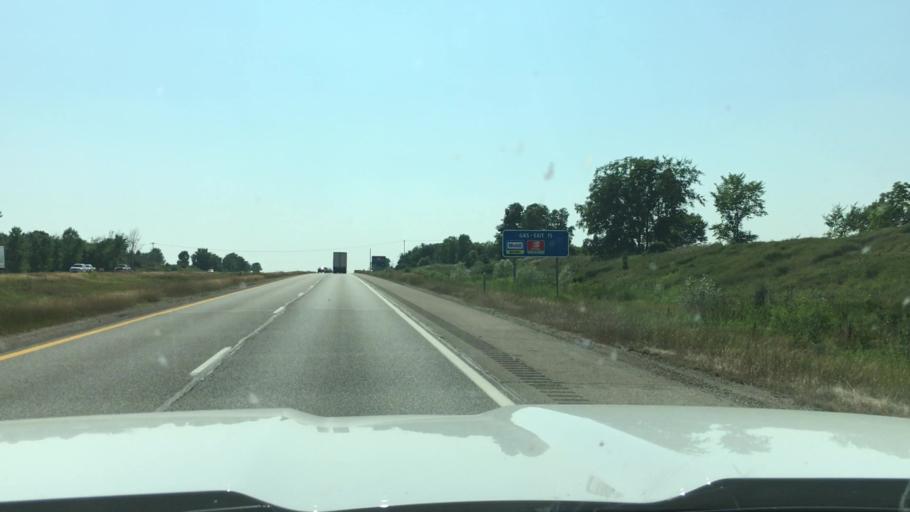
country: US
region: Michigan
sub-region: Kent County
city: Caledonia
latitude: 42.8562
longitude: -85.5133
